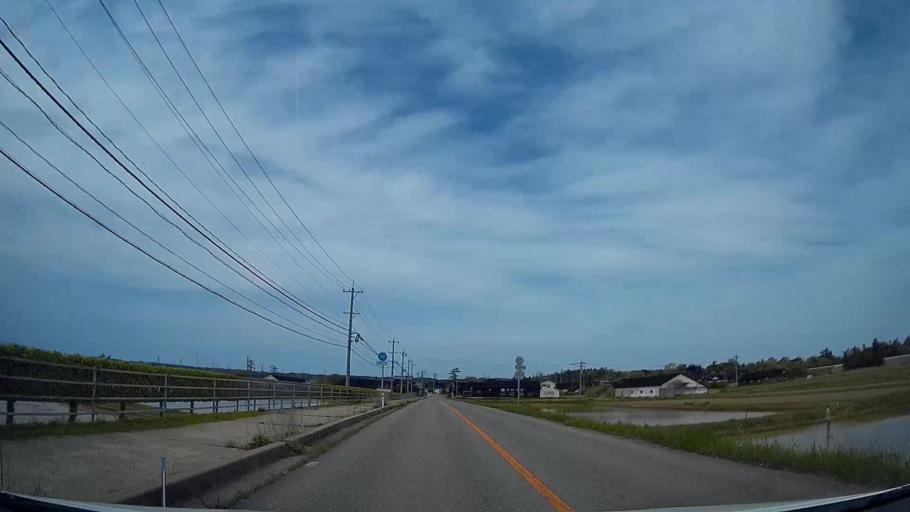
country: JP
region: Ishikawa
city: Hakui
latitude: 37.0216
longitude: 136.7472
